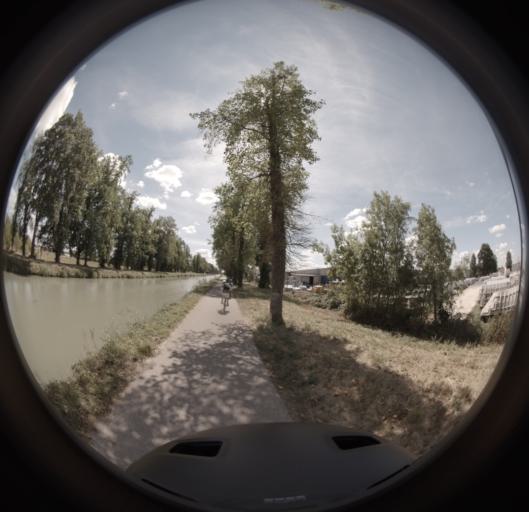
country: FR
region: Midi-Pyrenees
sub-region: Departement du Tarn-et-Garonne
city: Castelsarrasin
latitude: 44.0620
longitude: 1.1028
